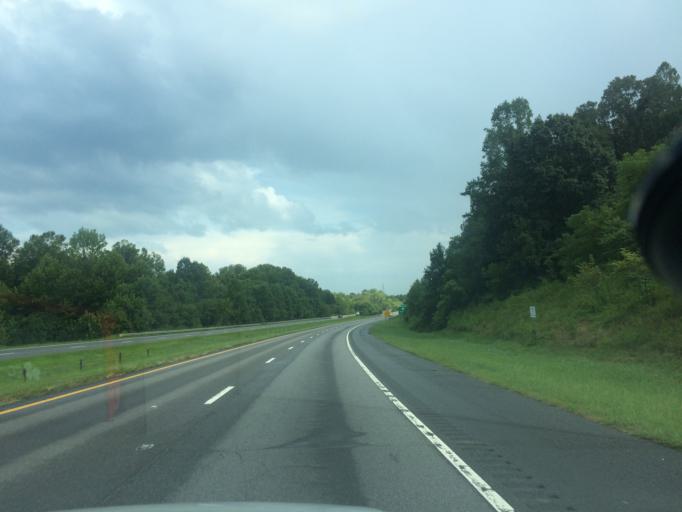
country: US
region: North Carolina
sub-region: Catawba County
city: Mountain View
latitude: 35.6461
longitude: -81.3064
